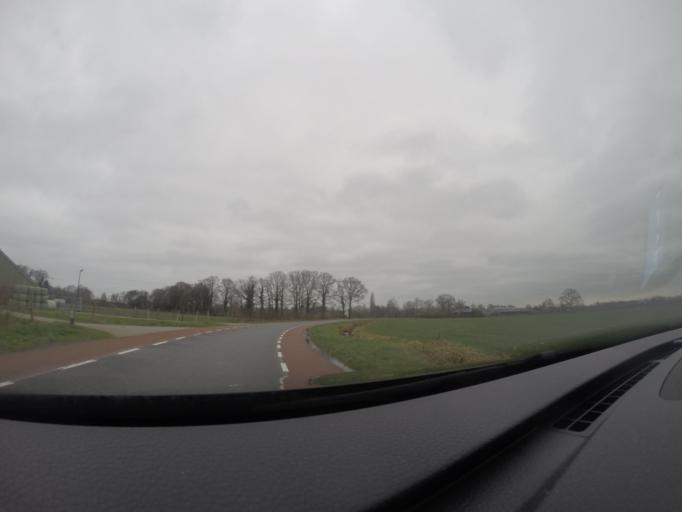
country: NL
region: Overijssel
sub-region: Gemeente Hof van Twente
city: Diepenheim
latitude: 52.1751
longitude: 6.5290
